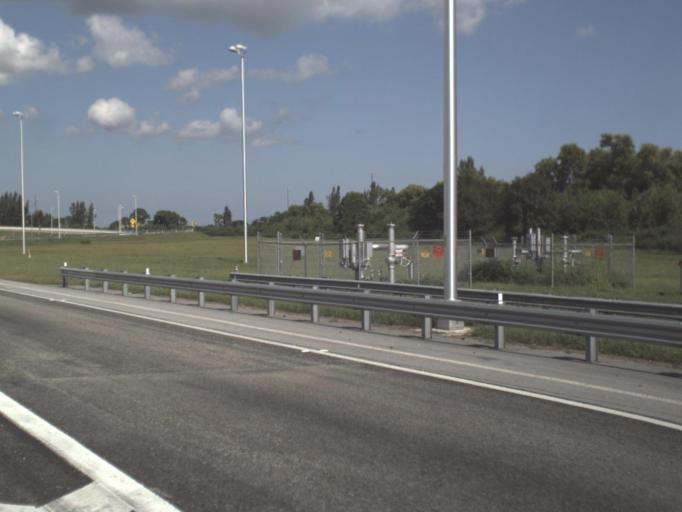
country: US
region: Florida
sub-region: Palm Beach County
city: Limestone Creek
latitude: 26.9356
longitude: -80.1541
